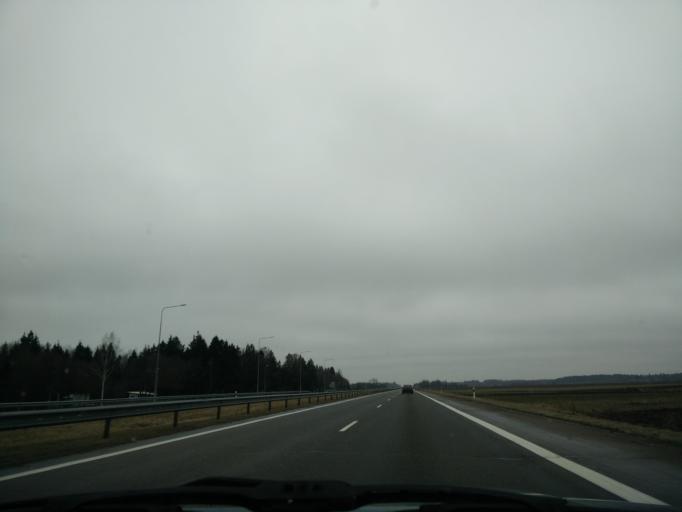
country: LT
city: Raseiniai
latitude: 55.3780
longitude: 22.9333
